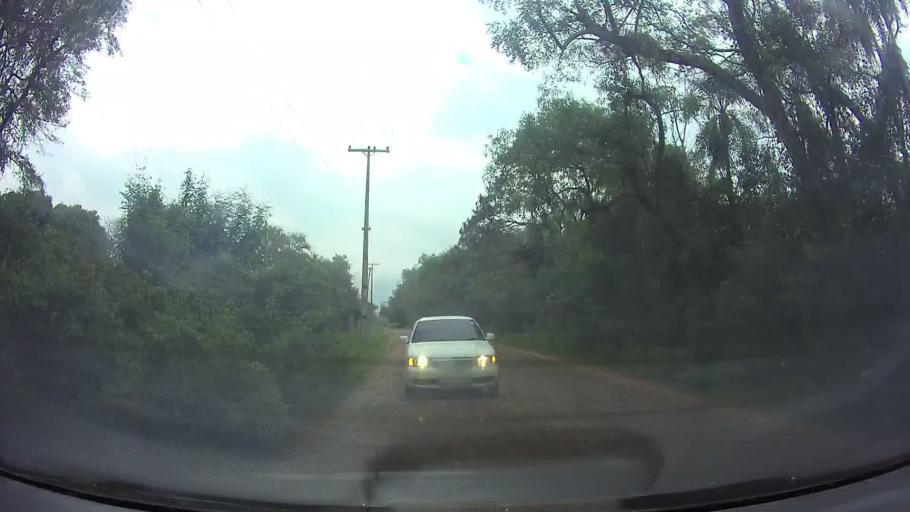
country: PY
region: Cordillera
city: Arroyos y Esteros
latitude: -25.0272
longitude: -57.1098
